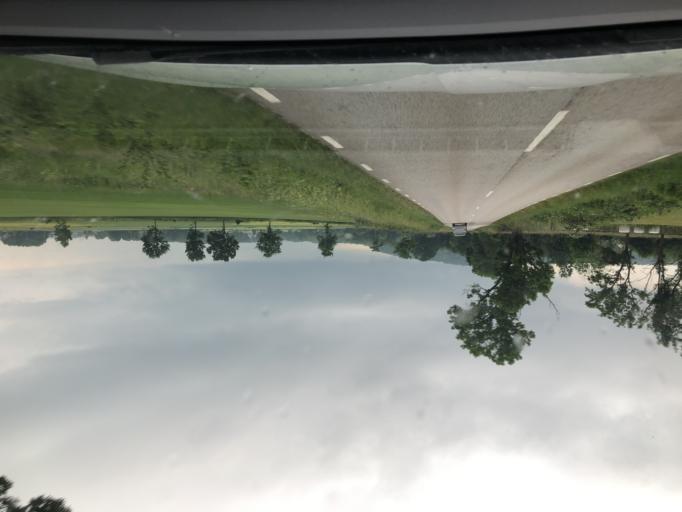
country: SE
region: Blekinge
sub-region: Solvesborgs Kommun
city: Soelvesborg
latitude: 56.0836
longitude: 14.6073
